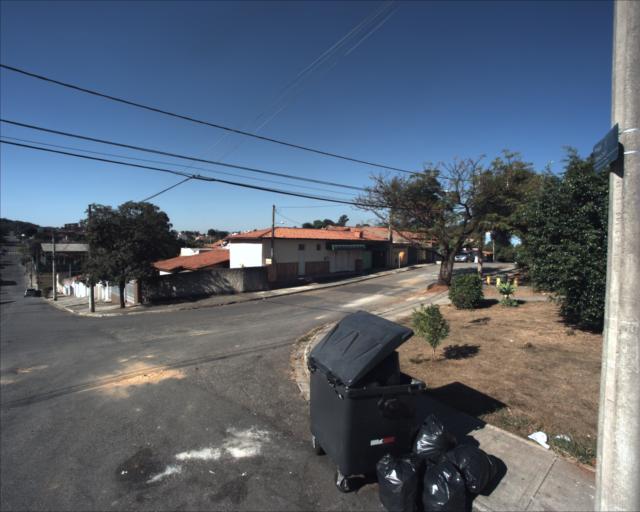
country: BR
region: Sao Paulo
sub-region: Sorocaba
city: Sorocaba
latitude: -23.5082
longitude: -47.4261
